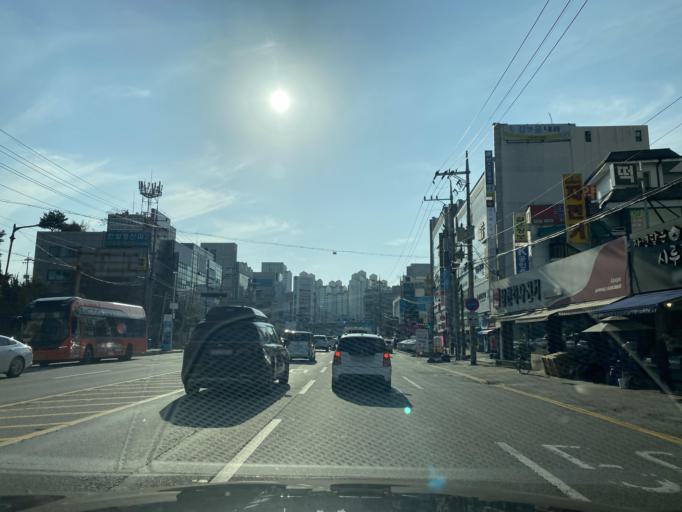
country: KR
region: Chungcheongnam-do
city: Cheonan
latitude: 36.7970
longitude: 127.1296
